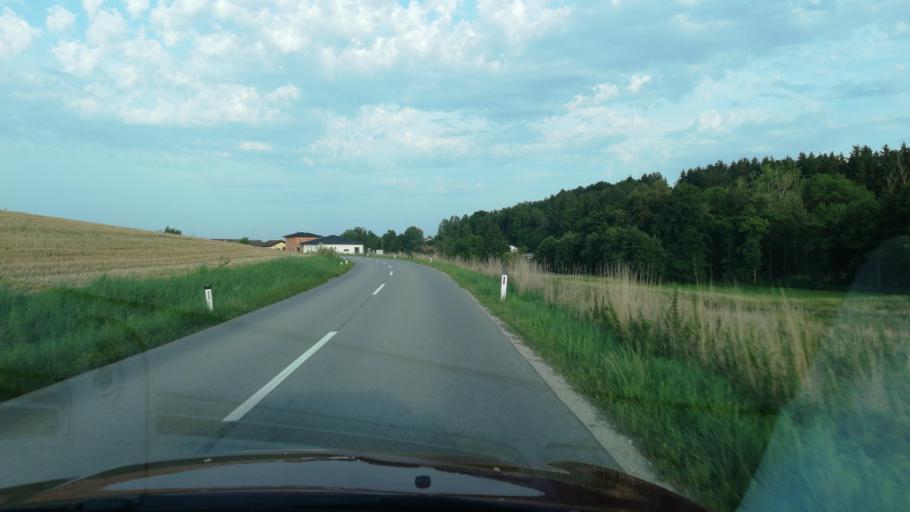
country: AT
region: Upper Austria
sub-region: Wels-Land
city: Edt bei Lambach
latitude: 48.1281
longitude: 13.8925
